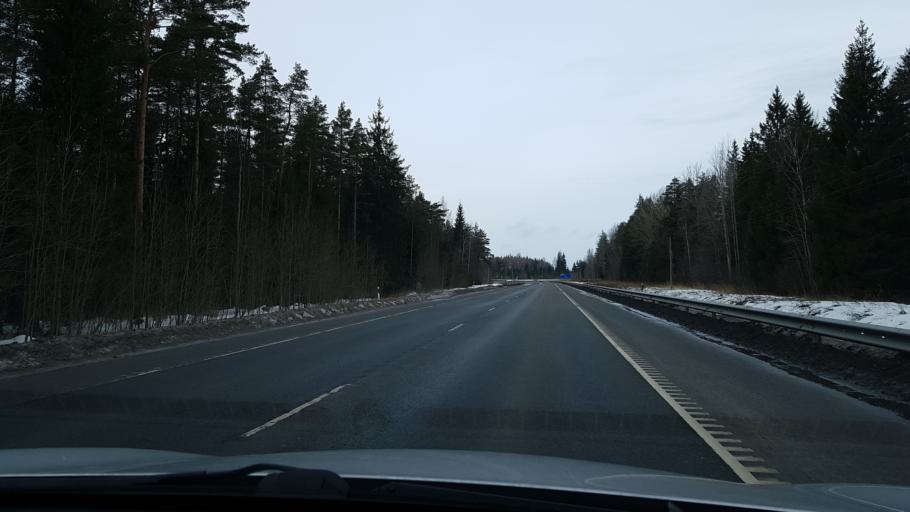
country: EE
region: Tartu
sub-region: Tartu linn
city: Tartu
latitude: 58.4046
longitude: 26.6544
